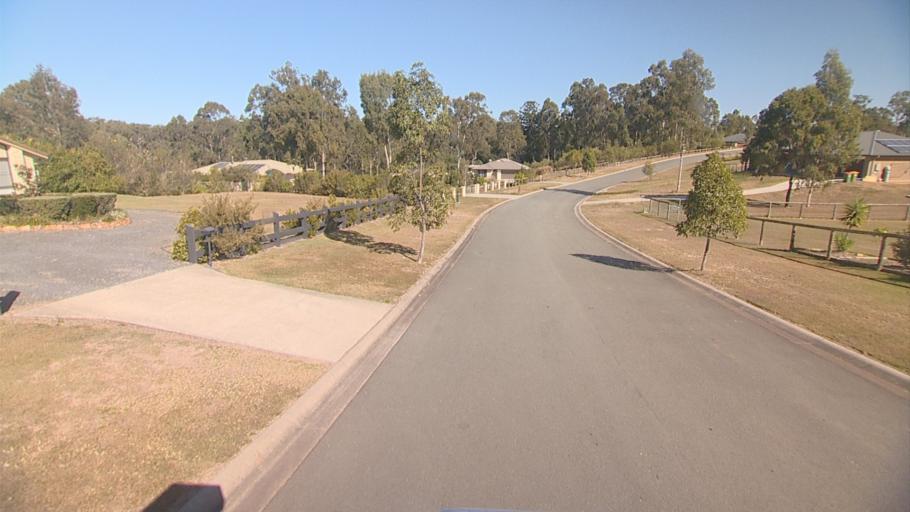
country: AU
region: Queensland
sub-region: Logan
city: Cedar Vale
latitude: -27.8714
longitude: 153.0360
